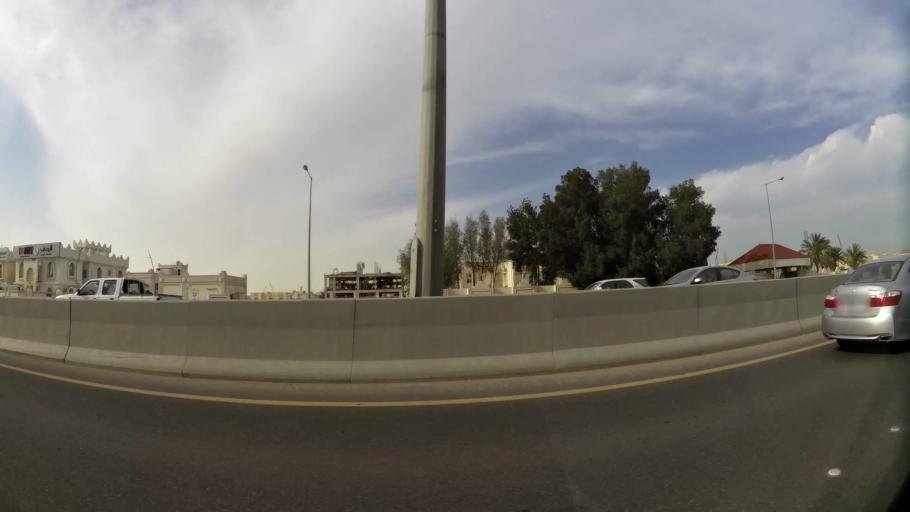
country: QA
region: Baladiyat ad Dawhah
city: Doha
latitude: 25.2543
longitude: 51.5153
